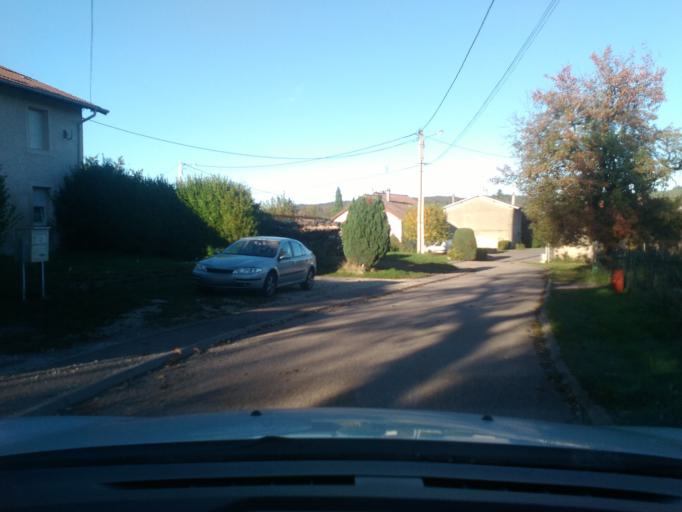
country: FR
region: Lorraine
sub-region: Departement des Vosges
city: Jeanmenil
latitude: 48.2900
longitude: 6.7088
